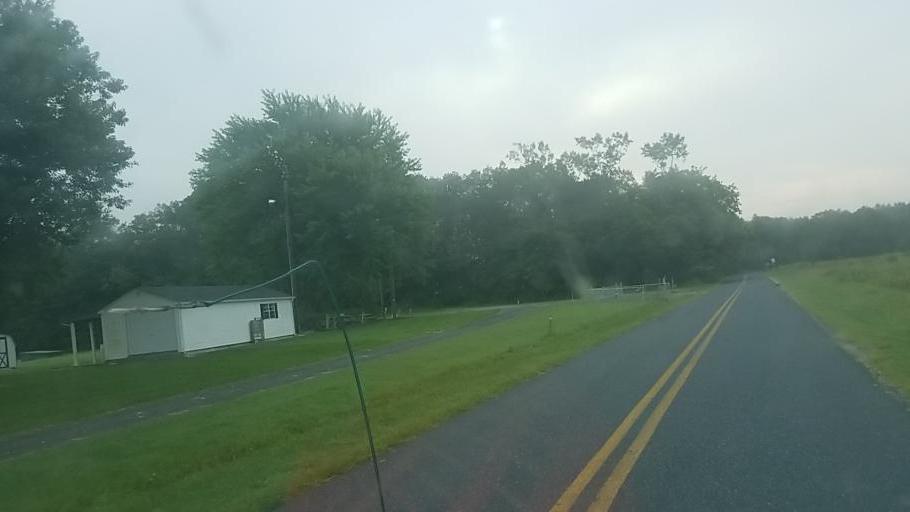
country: US
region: Maryland
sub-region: Wicomico County
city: Pittsville
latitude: 38.4150
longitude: -75.4917
